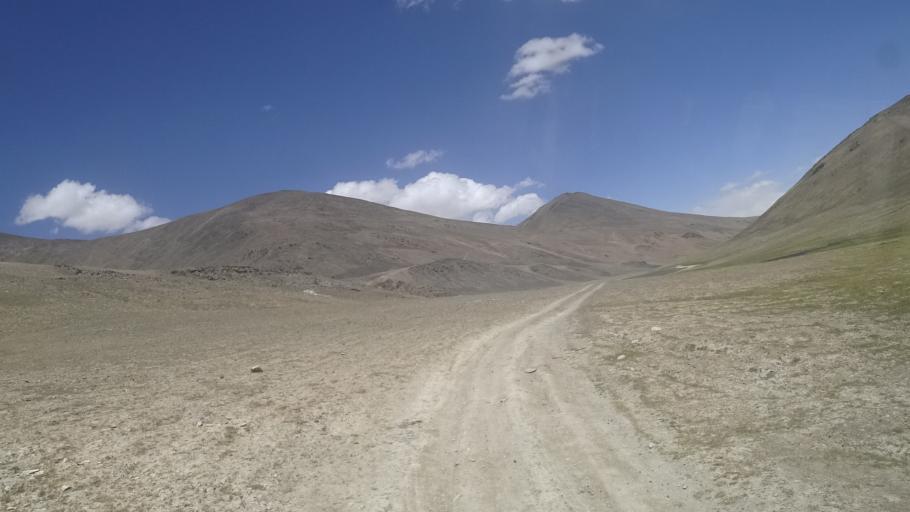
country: TJ
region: Gorno-Badakhshan
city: Murghob
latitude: 37.5182
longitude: 74.0586
